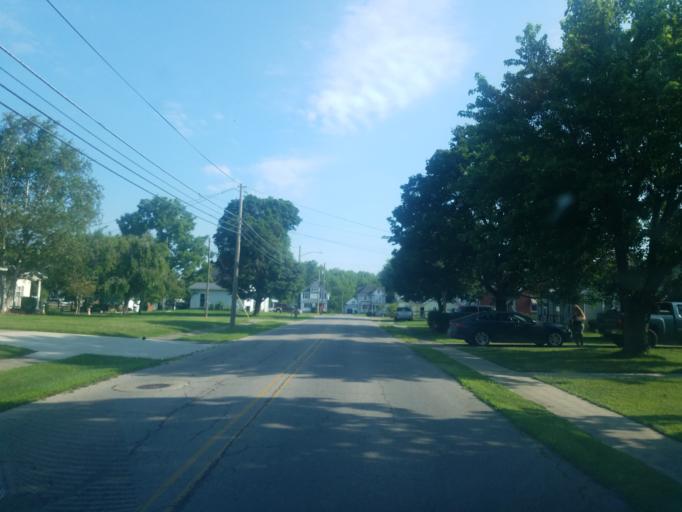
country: US
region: Ohio
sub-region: Richland County
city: Shelby
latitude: 40.8800
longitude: -82.6772
